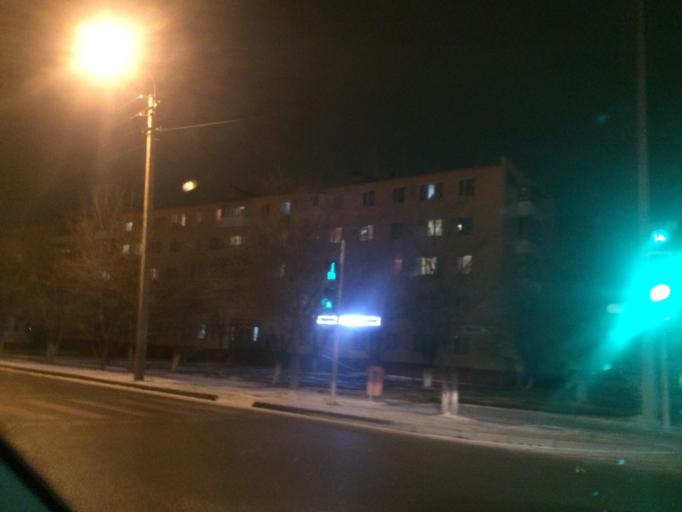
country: KZ
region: Astana Qalasy
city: Astana
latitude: 51.1867
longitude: 71.4212
